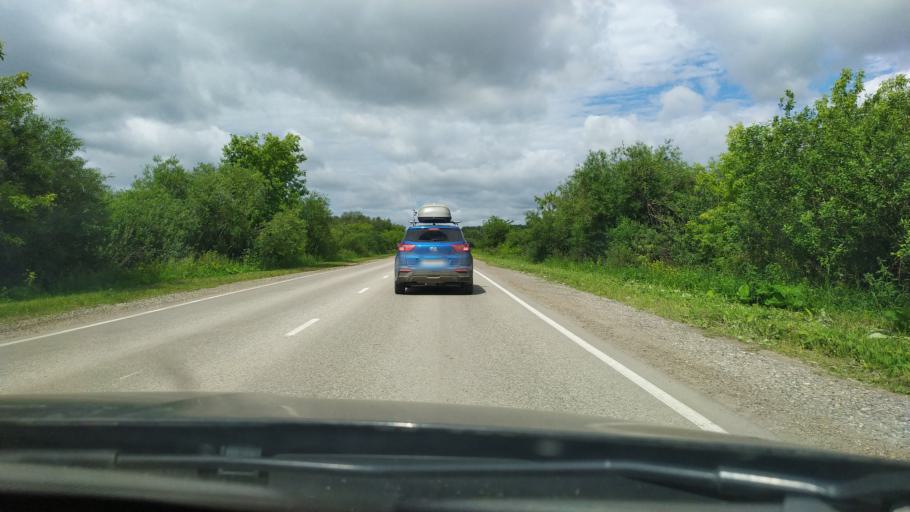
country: RU
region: Perm
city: Kondratovo
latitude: 57.9303
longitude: 56.0981
